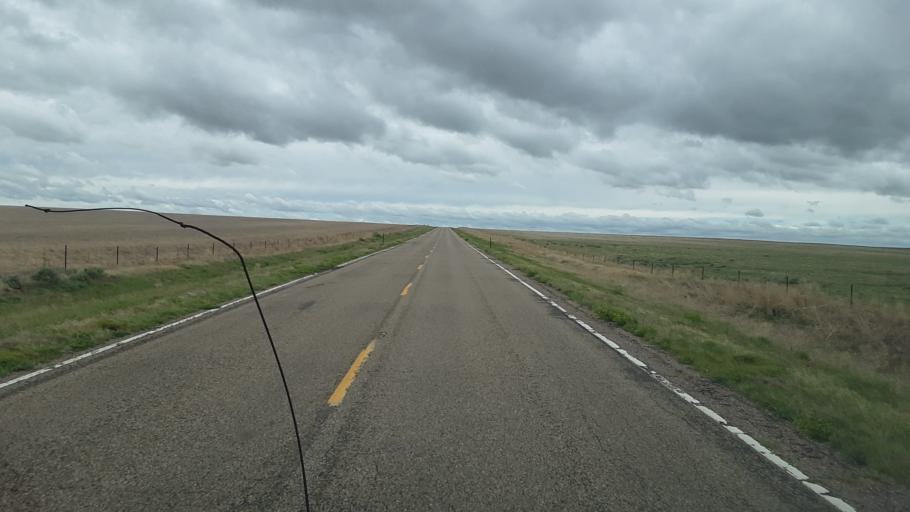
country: US
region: Colorado
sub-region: Lincoln County
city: Hugo
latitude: 38.8513
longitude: -103.6303
